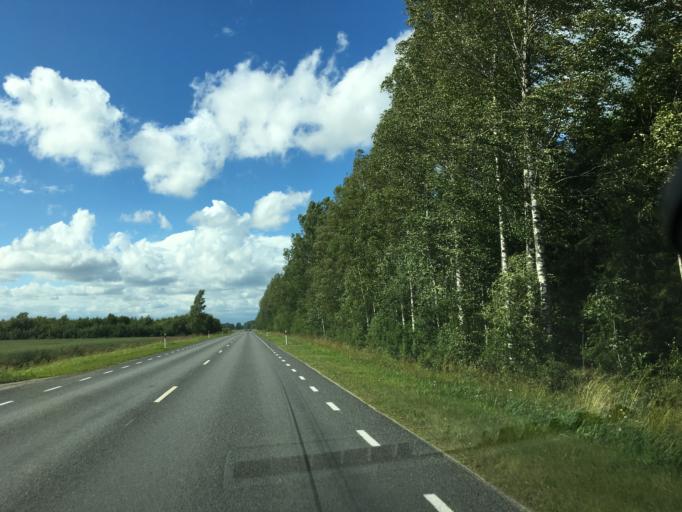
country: EE
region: Paernumaa
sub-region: Vaendra vald (alev)
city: Vandra
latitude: 58.5967
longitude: 25.1474
